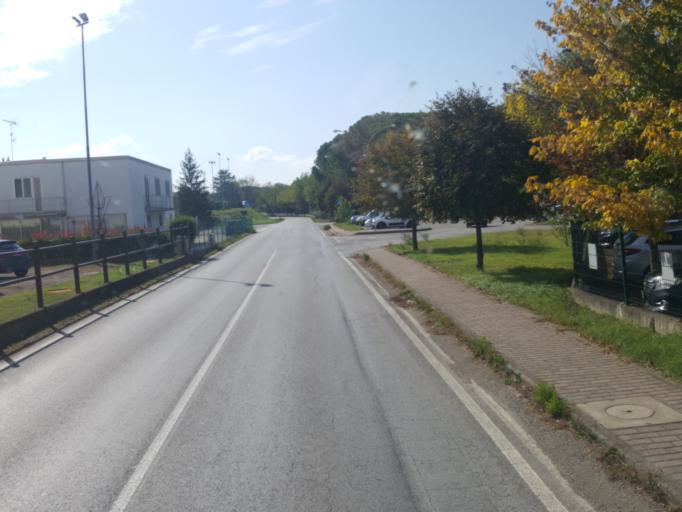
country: IT
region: Tuscany
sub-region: Provincia di Siena
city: Colle di Val d'Elsa
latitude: 43.4056
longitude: 11.1387
